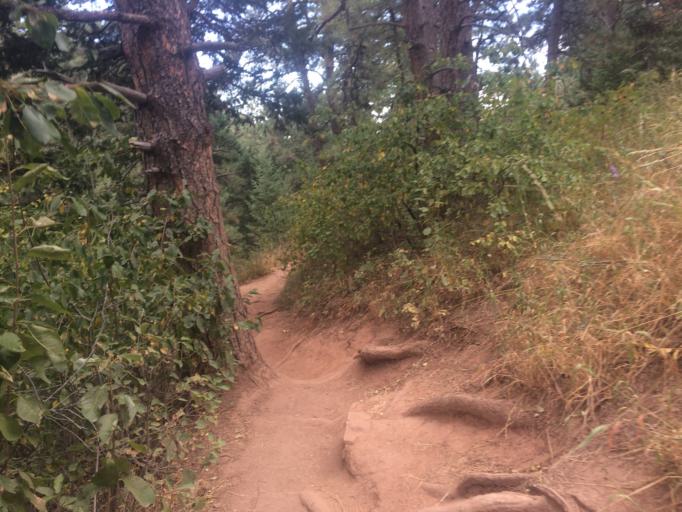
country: US
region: Colorado
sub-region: Boulder County
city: Boulder
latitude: 39.9763
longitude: -105.2840
